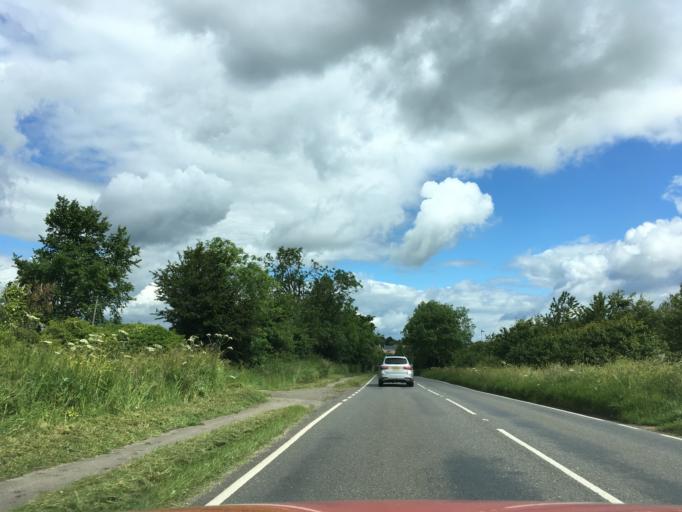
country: GB
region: England
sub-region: Oxfordshire
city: Chipping Norton
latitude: 51.9281
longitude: -1.5414
